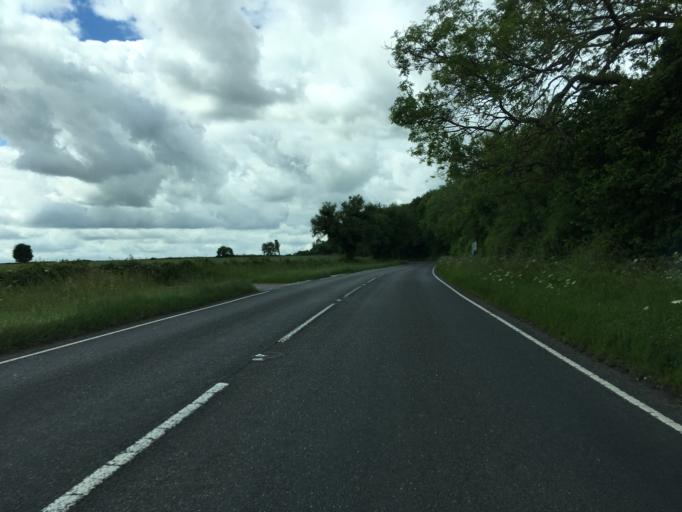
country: GB
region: England
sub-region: Oxfordshire
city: Chipping Norton
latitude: 51.8992
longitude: -1.5602
